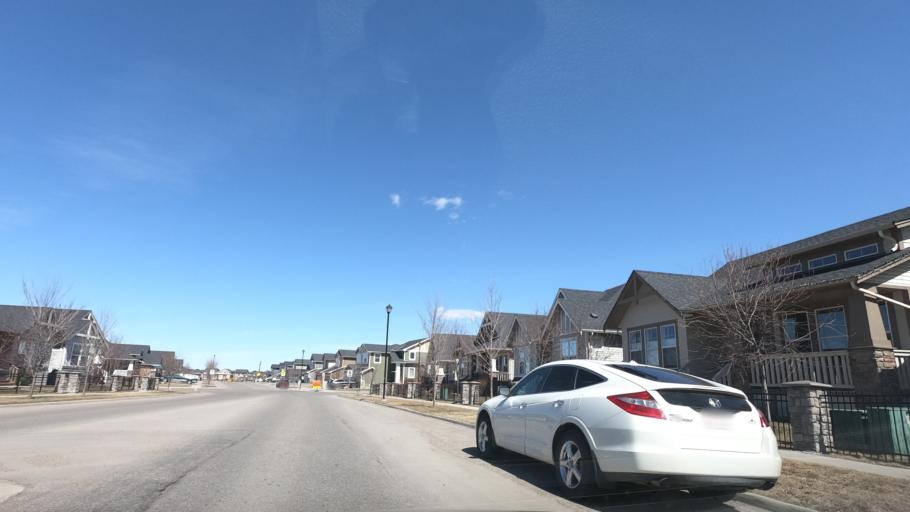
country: CA
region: Alberta
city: Airdrie
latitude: 51.3007
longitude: -114.0330
